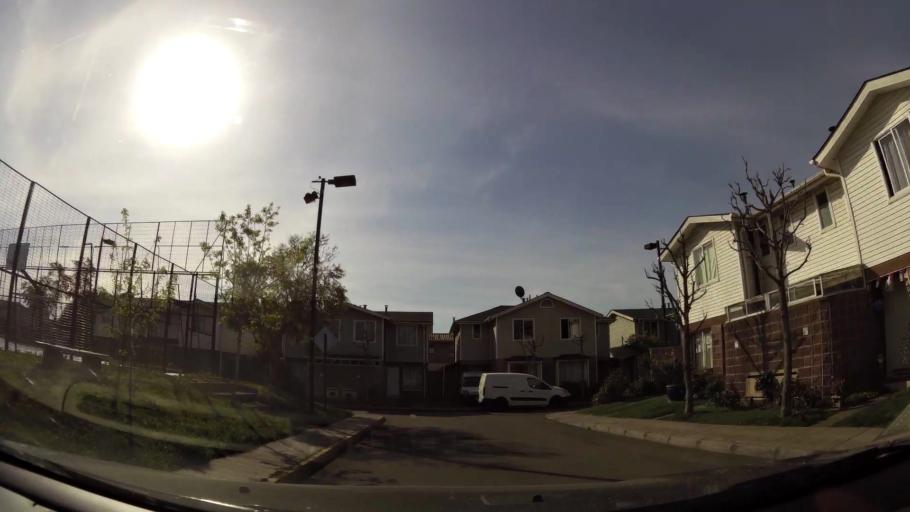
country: CL
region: Santiago Metropolitan
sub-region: Provincia de Cordillera
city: Puente Alto
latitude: -33.5900
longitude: -70.5589
